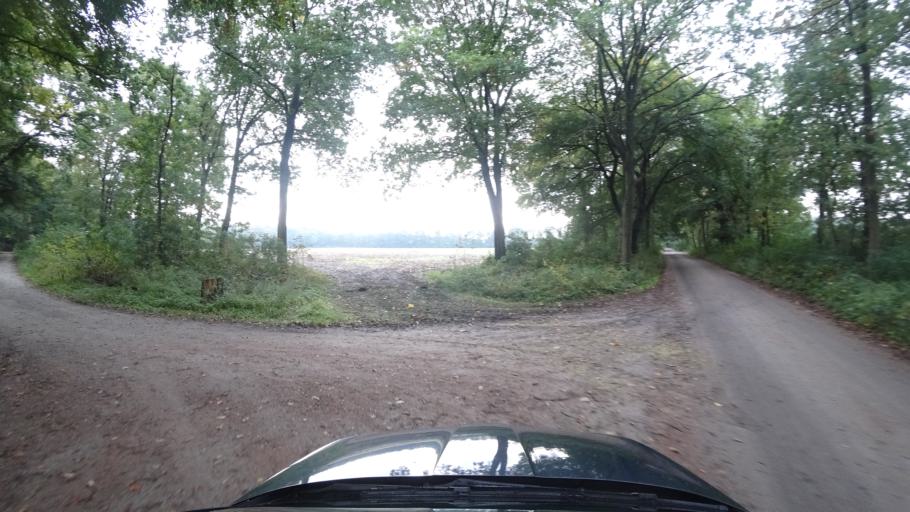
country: NL
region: Gelderland
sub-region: Gemeente Renkum
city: Wolfheze
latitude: 52.0062
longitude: 5.7749
